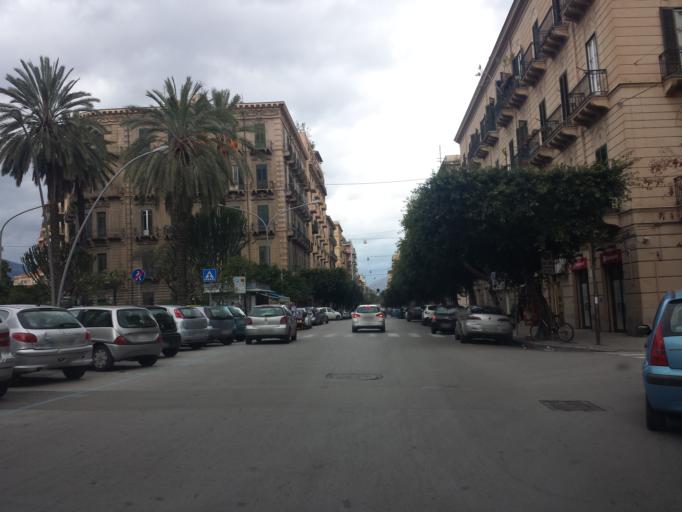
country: IT
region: Sicily
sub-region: Palermo
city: Palermo
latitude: 38.1223
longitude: 13.3515
